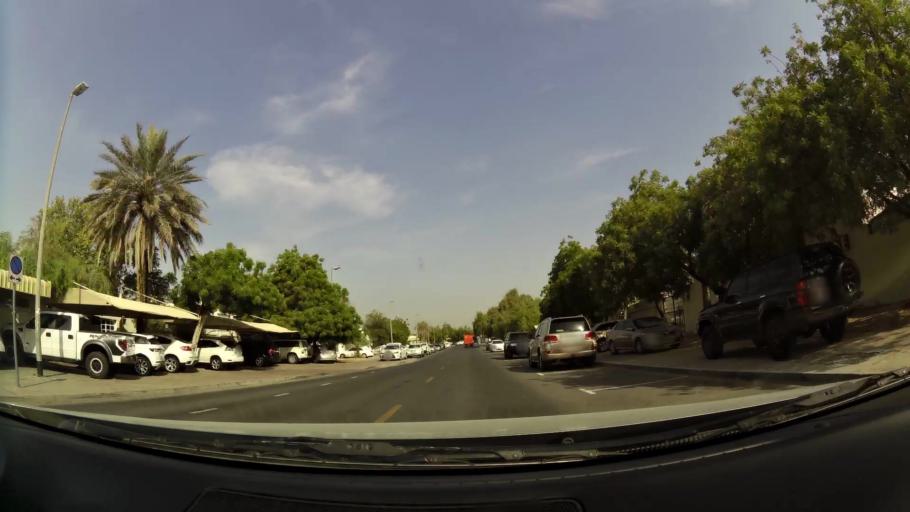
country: AE
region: Ash Shariqah
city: Sharjah
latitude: 25.2188
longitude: 55.3888
